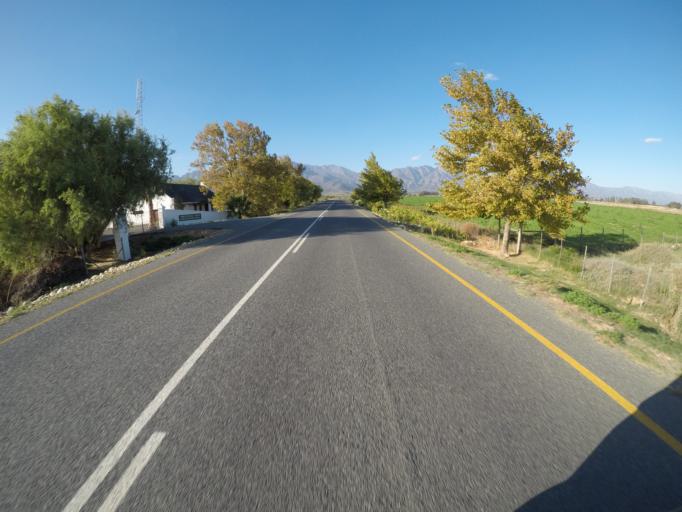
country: ZA
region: Western Cape
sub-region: Cape Winelands District Municipality
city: Worcester
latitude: -33.6765
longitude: 19.5300
